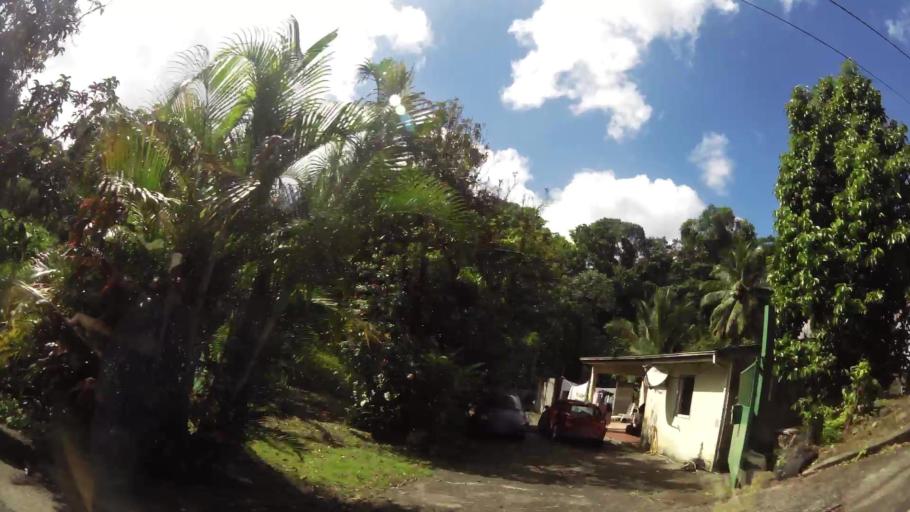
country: MQ
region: Martinique
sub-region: Martinique
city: Saint-Pierre
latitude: 14.7570
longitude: -61.1631
